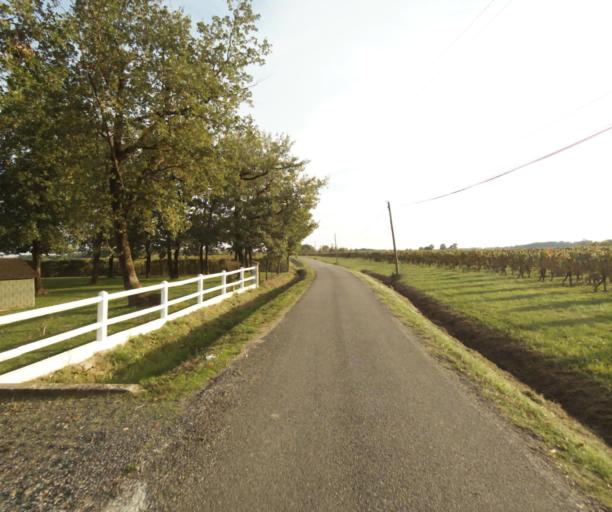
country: FR
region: Midi-Pyrenees
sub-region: Departement du Tarn-et-Garonne
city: Campsas
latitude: 43.9092
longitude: 1.3387
